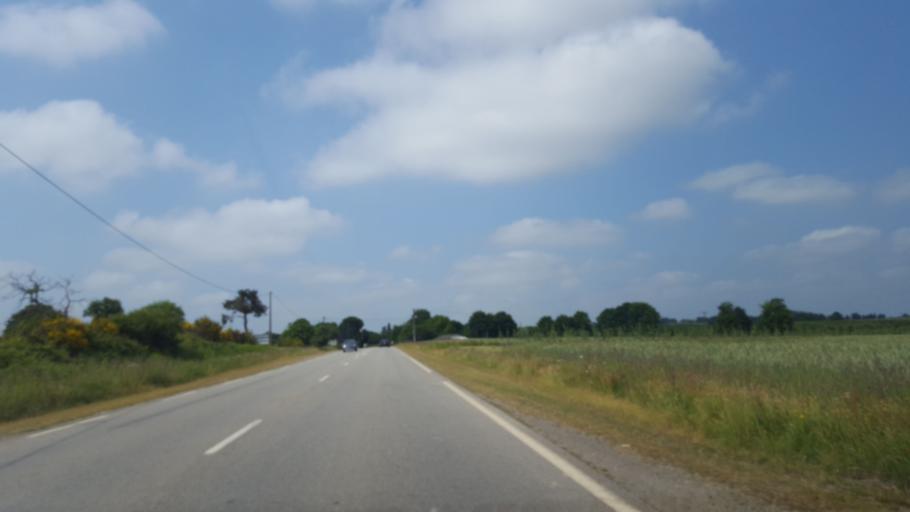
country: FR
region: Brittany
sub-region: Departement d'Ille-et-Vilaine
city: Maure-de-Bretagne
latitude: 47.9197
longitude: -1.9678
